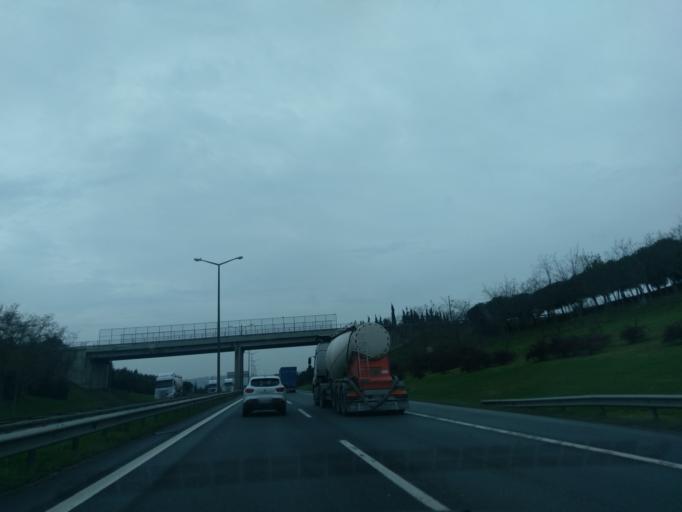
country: TR
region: Istanbul
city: Silivri
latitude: 41.1129
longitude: 28.2624
